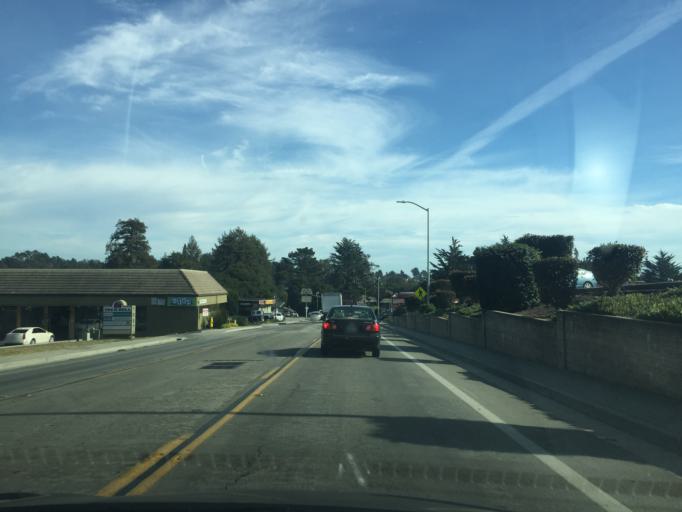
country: US
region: California
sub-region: Santa Cruz County
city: Aptos
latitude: 36.9783
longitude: -121.9071
